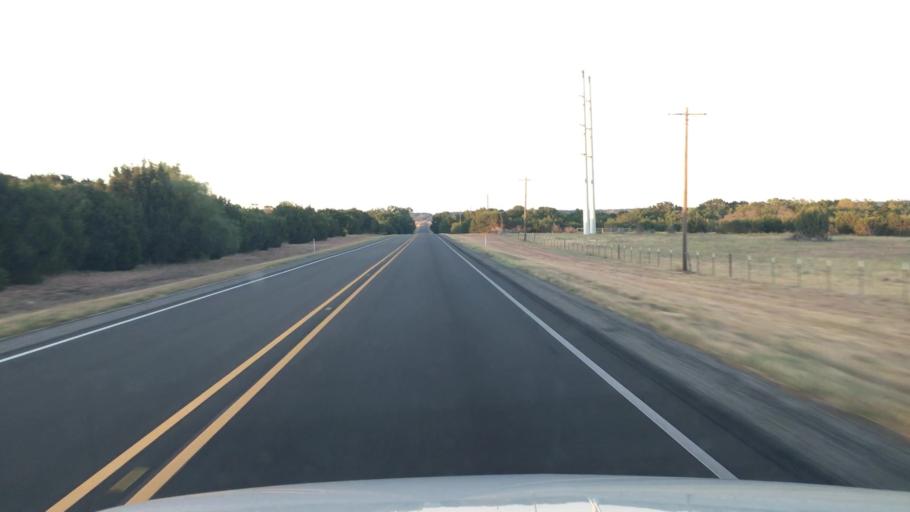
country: US
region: Texas
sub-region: Hamilton County
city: Hico
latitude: 32.0628
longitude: -97.9938
